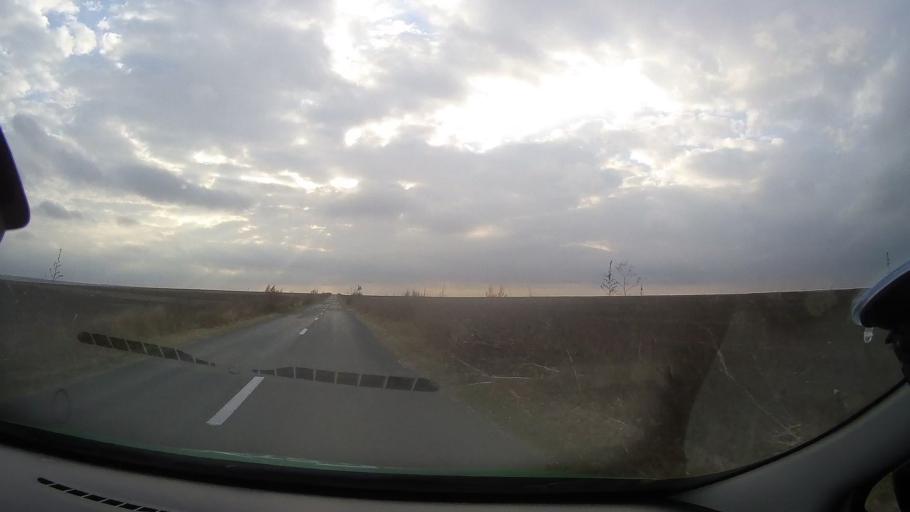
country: RO
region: Constanta
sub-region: Comuna Pestera
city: Pestera
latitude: 44.1299
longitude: 28.1143
